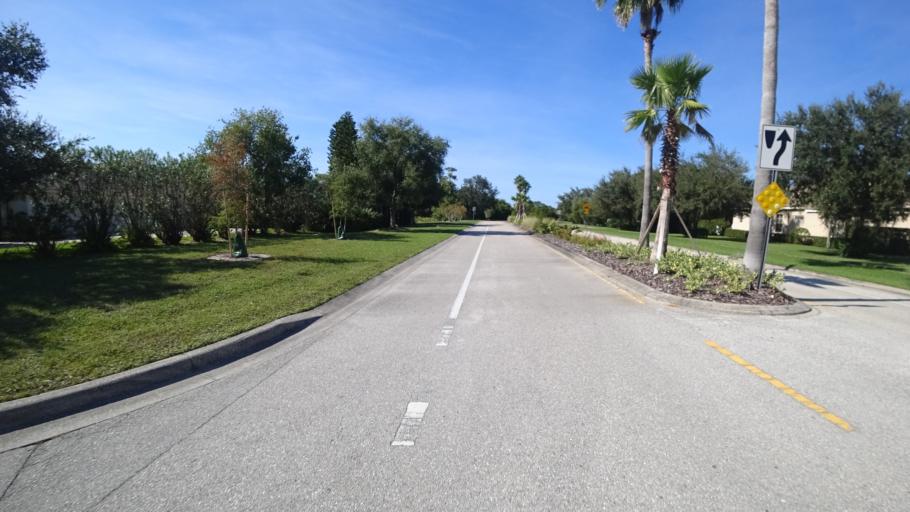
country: US
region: Florida
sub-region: Sarasota County
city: The Meadows
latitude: 27.4060
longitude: -82.4380
